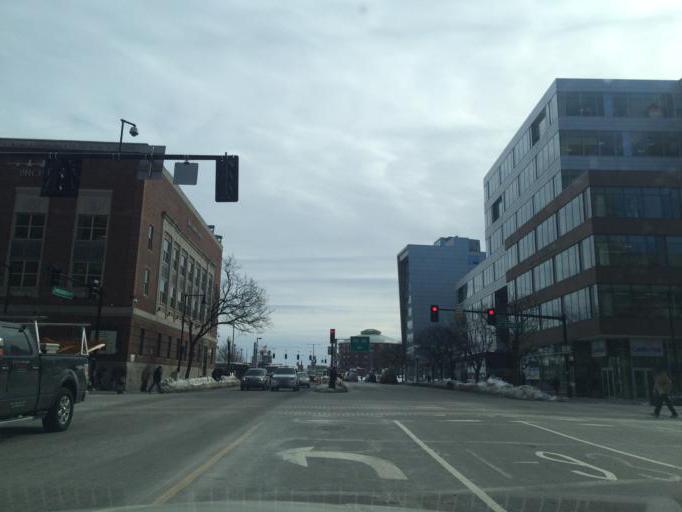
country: US
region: Massachusetts
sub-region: Suffolk County
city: South Boston
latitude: 42.3338
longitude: -71.0736
